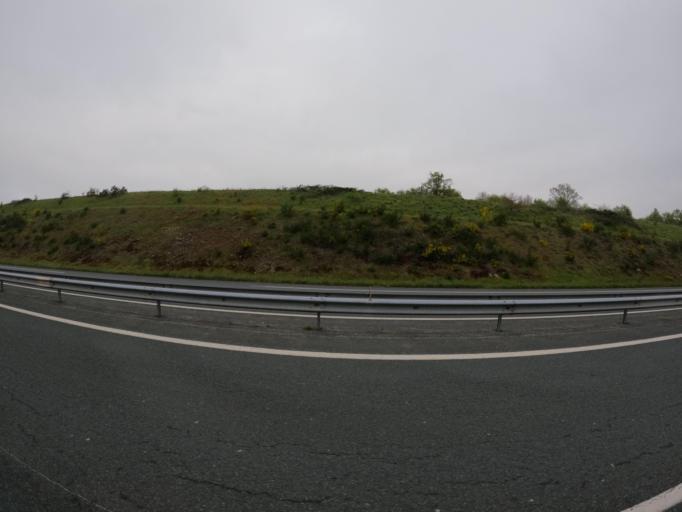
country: FR
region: Pays de la Loire
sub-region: Departement de Maine-et-Loire
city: La Tessoualle
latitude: 47.0278
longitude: -0.8631
